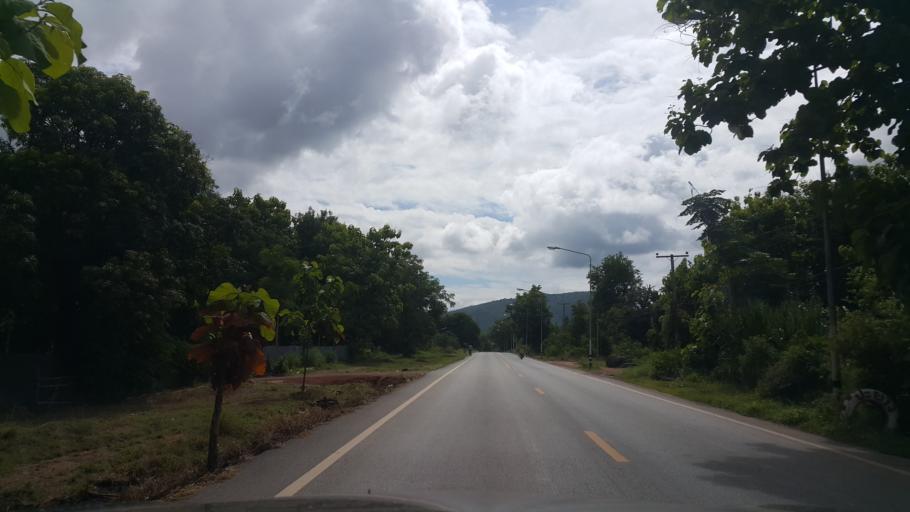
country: TH
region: Uttaradit
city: Thong Saen Khan
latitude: 17.3967
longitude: 100.3022
